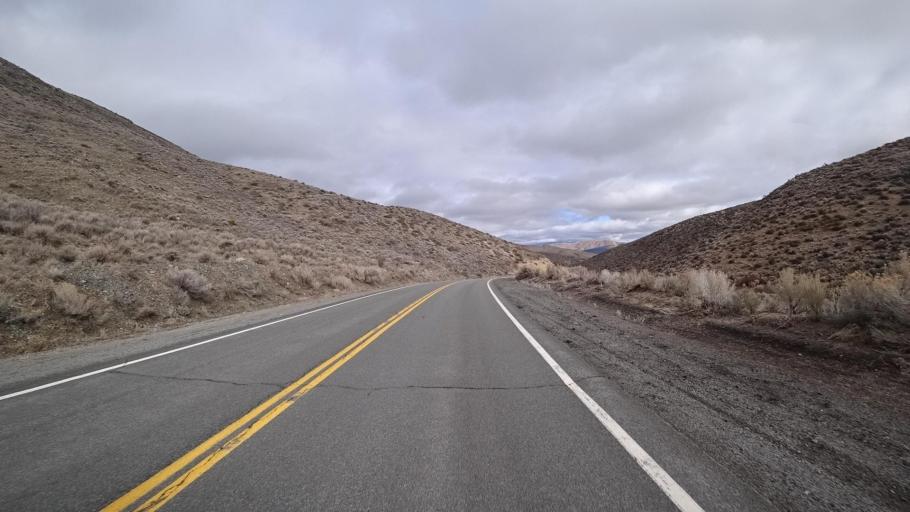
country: US
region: Nevada
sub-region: Washoe County
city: Cold Springs
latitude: 39.8174
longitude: -119.9357
